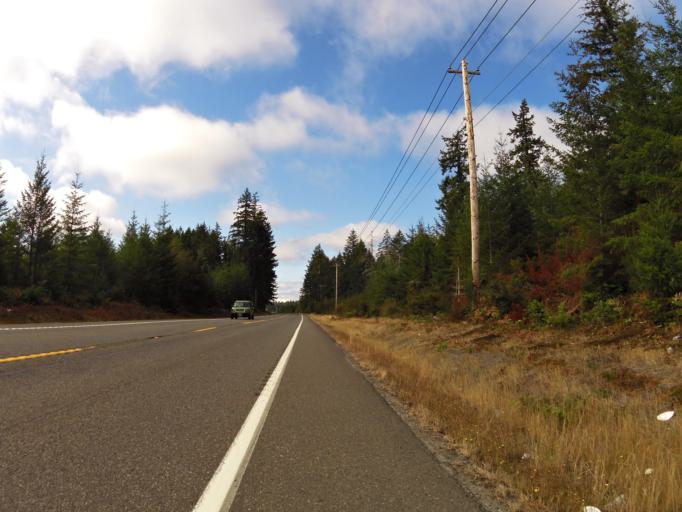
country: US
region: Washington
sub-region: Mason County
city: Allyn
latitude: 47.3394
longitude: -122.8661
